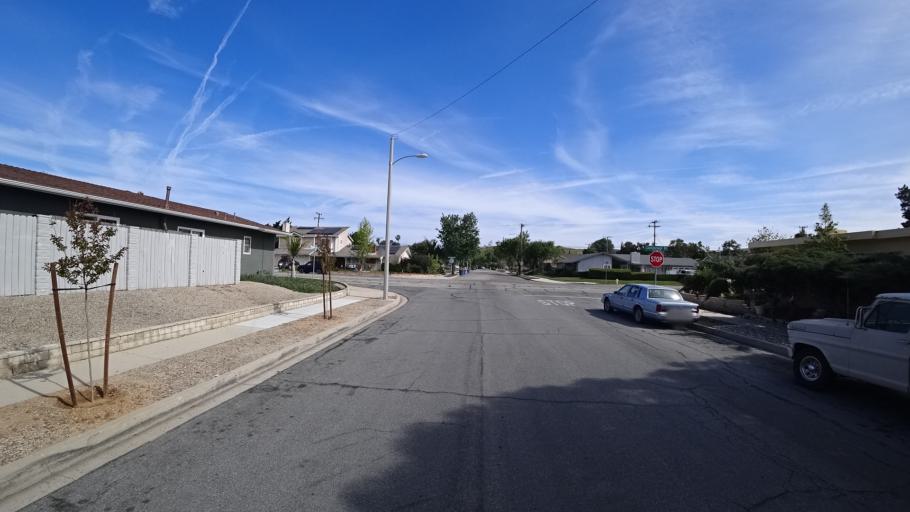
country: US
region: California
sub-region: Ventura County
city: Thousand Oaks
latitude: 34.1961
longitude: -118.8799
